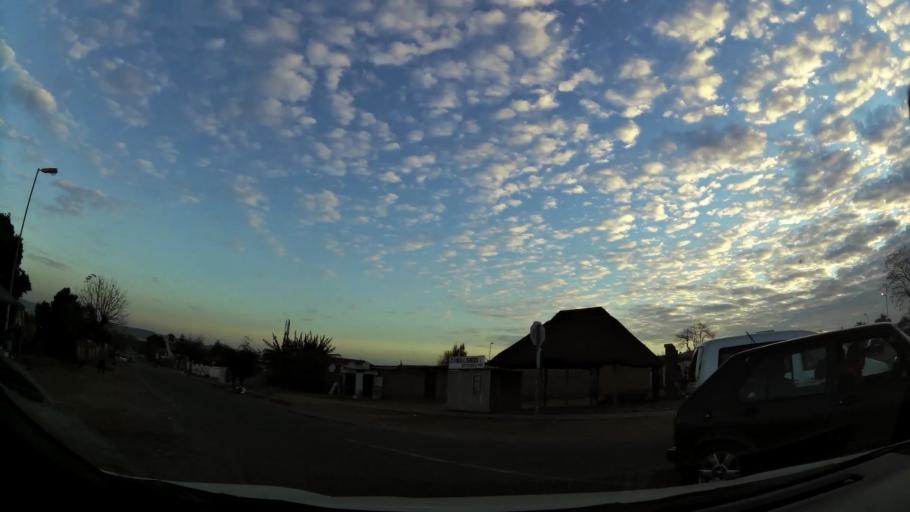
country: ZA
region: Gauteng
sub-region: City of Tshwane Metropolitan Municipality
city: Pretoria
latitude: -25.7027
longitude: 28.3326
